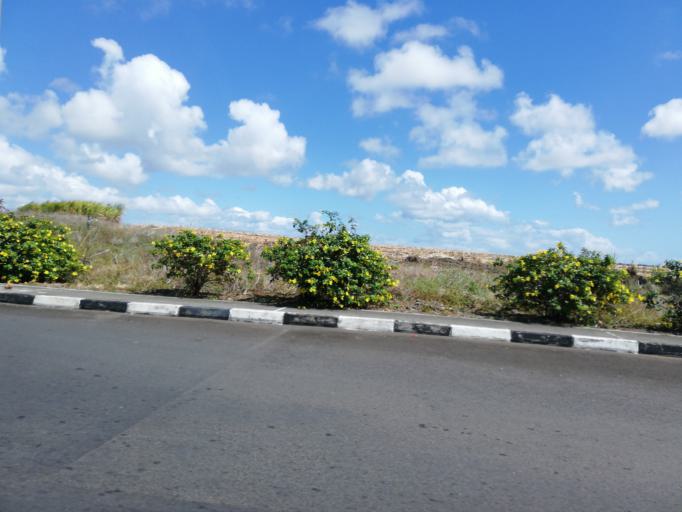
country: MU
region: Riviere du Rempart
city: Goodlands
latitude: -20.0318
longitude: 57.6417
